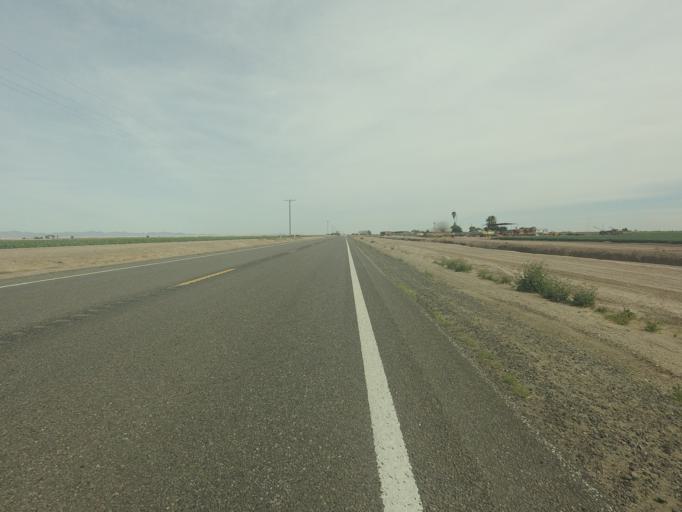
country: US
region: California
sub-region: Imperial County
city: Brawley
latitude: 32.9746
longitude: -115.3836
